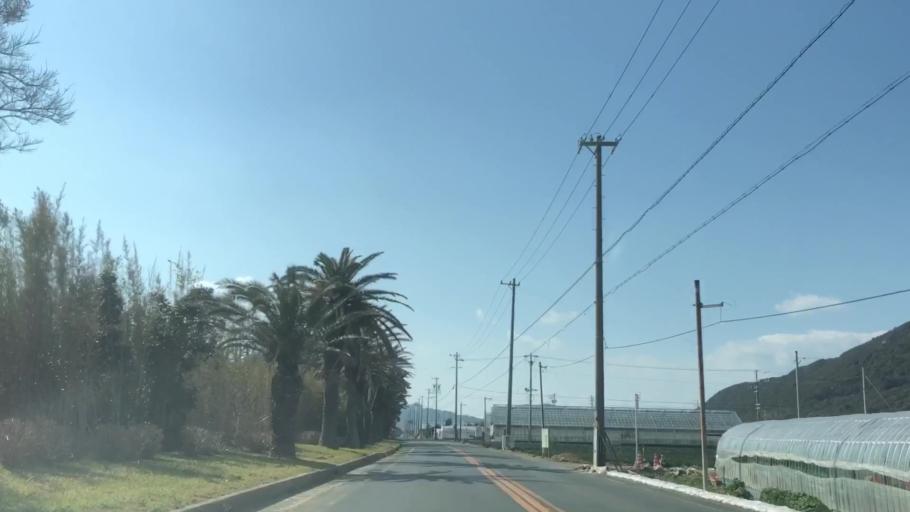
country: JP
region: Aichi
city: Toyohama
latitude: 34.5876
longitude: 137.0706
